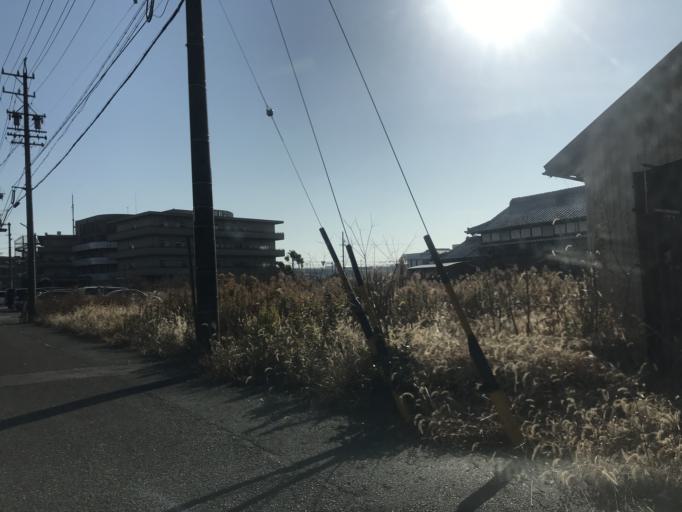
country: JP
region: Aichi
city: Iwakura
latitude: 35.2272
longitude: 136.8487
